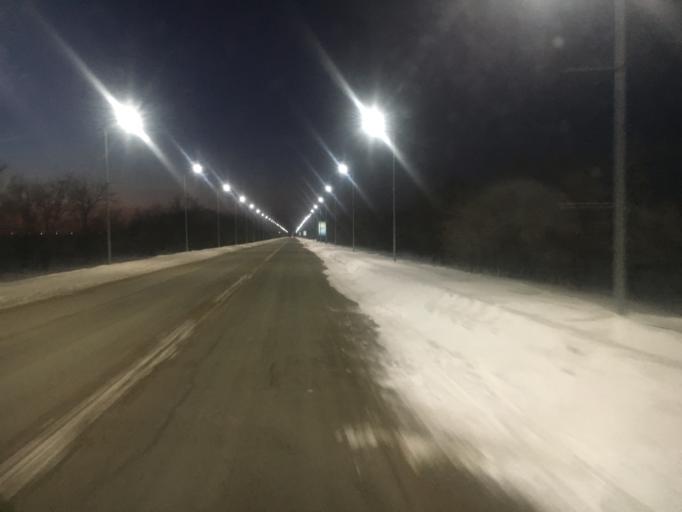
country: KZ
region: Batys Qazaqstan
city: Oral
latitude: 51.1561
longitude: 51.5355
